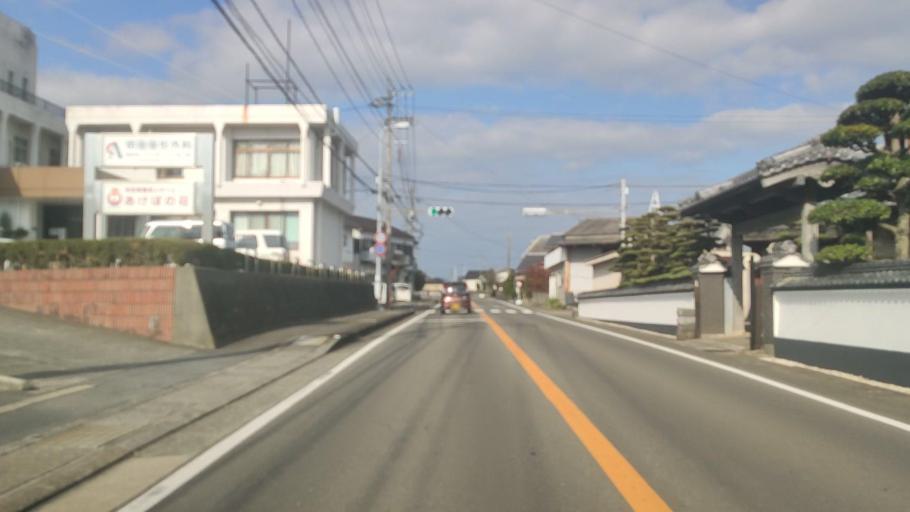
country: JP
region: Nagasaki
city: Shimabara
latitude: 32.6941
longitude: 130.3537
